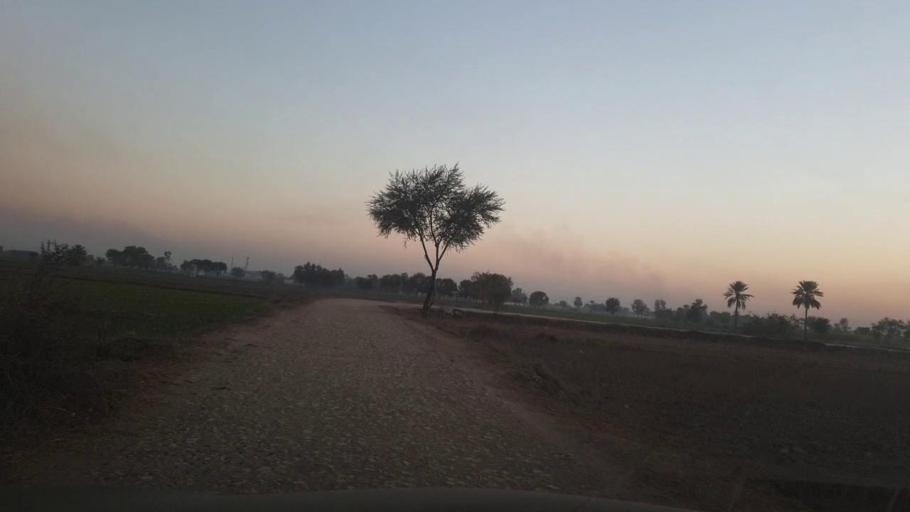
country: PK
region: Sindh
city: Ghotki
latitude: 28.0430
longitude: 69.3551
